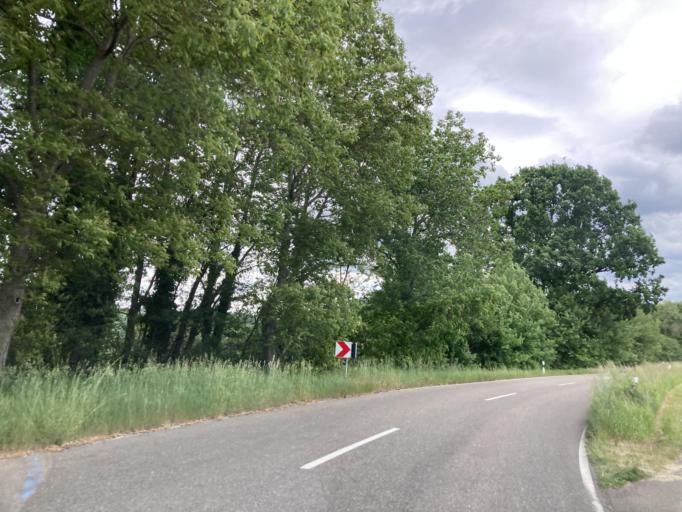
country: DE
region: Baden-Wuerttemberg
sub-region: Karlsruhe Region
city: Muggensturm
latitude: 48.8634
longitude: 8.2953
